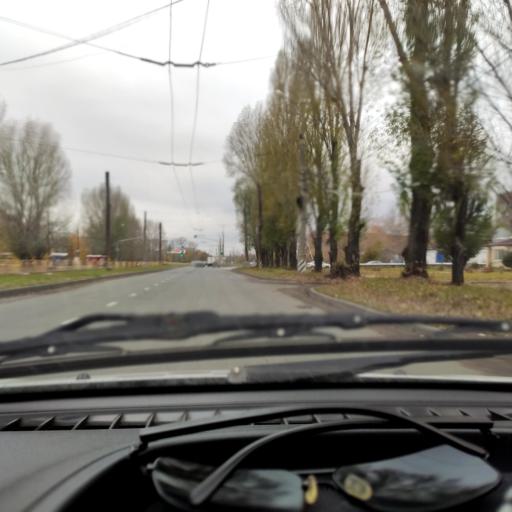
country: RU
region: Samara
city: Tol'yatti
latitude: 53.5115
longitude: 49.4588
